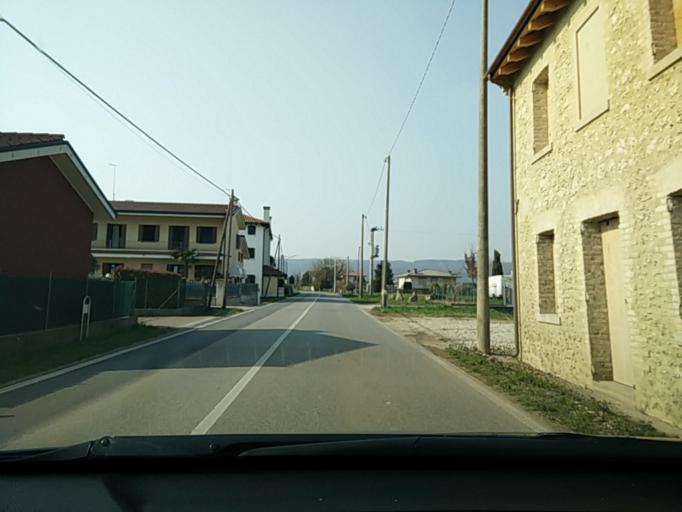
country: IT
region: Veneto
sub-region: Provincia di Treviso
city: Selva del Montello
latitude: 45.7692
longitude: 12.1487
